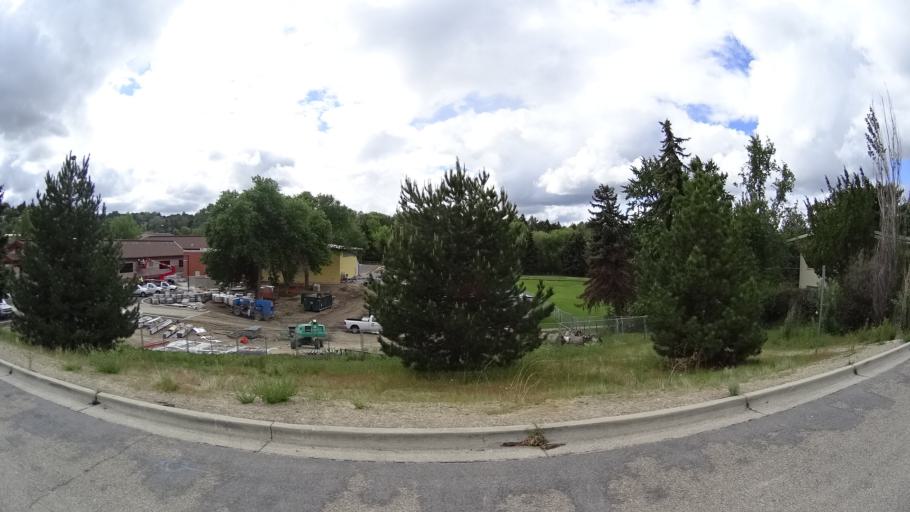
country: US
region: Idaho
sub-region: Ada County
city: Boise
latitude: 43.6507
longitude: -116.1962
